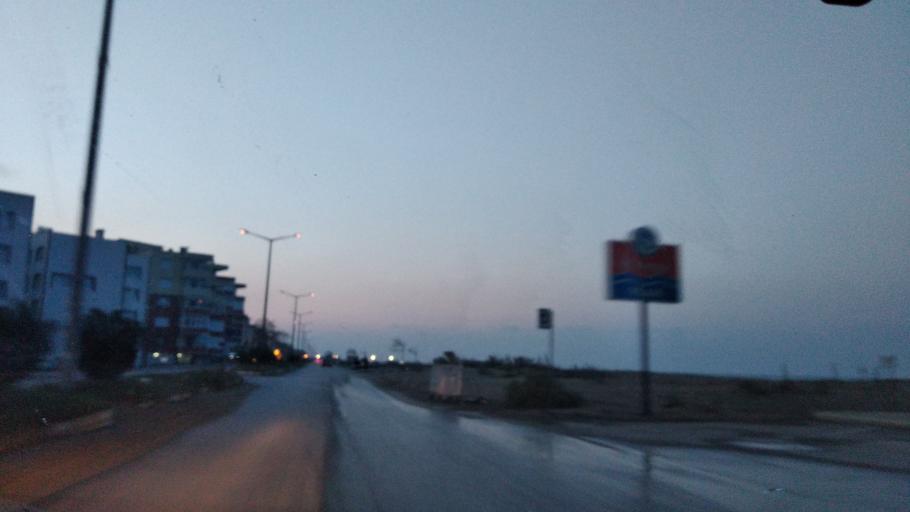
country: TR
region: Sakarya
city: Karasu
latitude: 41.1012
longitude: 30.7172
